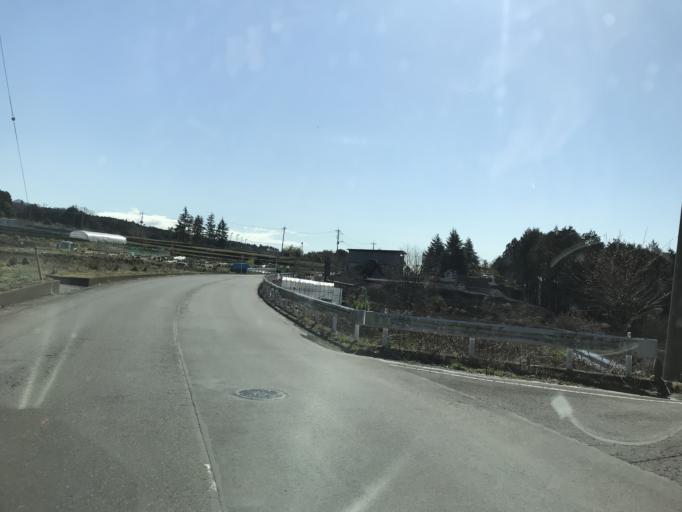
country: JP
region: Shizuoka
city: Fujinomiya
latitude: 35.2431
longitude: 138.6608
